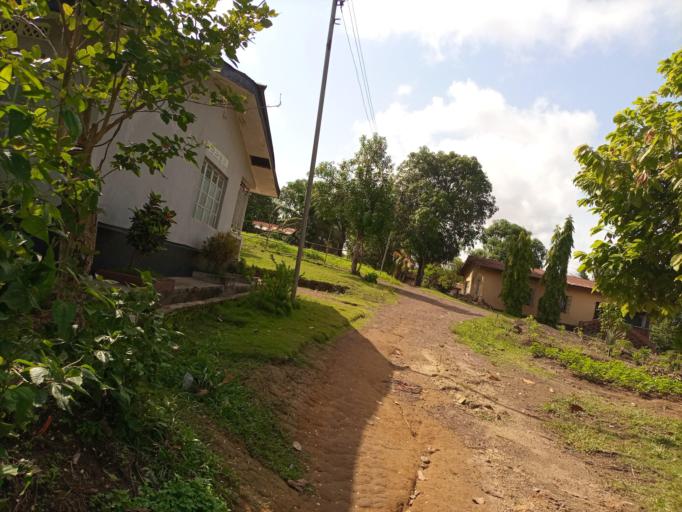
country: SL
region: Southern Province
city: Bo
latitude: 7.9656
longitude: -11.7673
